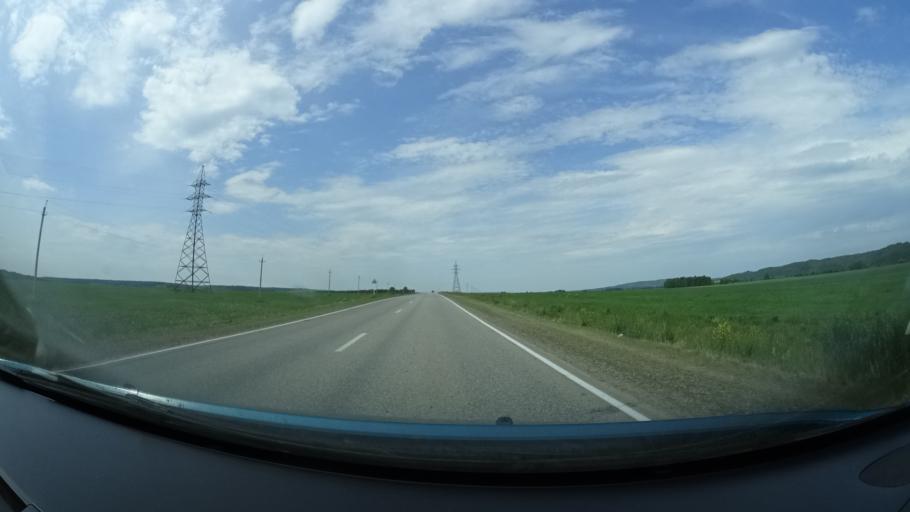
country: RU
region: Perm
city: Barda
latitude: 57.0069
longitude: 55.5641
